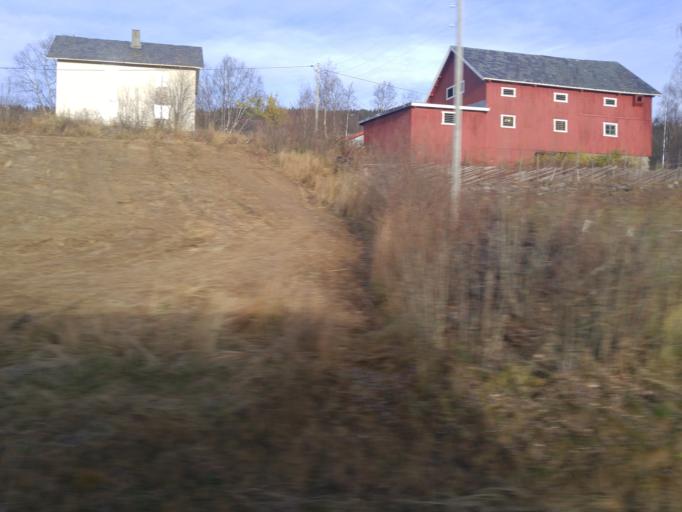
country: NO
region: Oppland
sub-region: Nord-Aurdal
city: Fagernes
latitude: 61.0630
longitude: 9.1620
